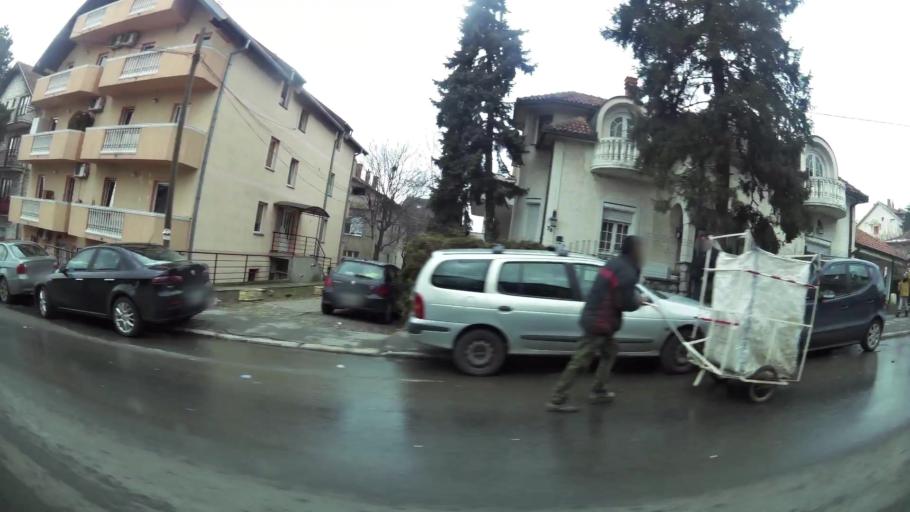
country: RS
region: Central Serbia
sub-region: Belgrade
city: Cukarica
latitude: 44.7543
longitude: 20.4051
